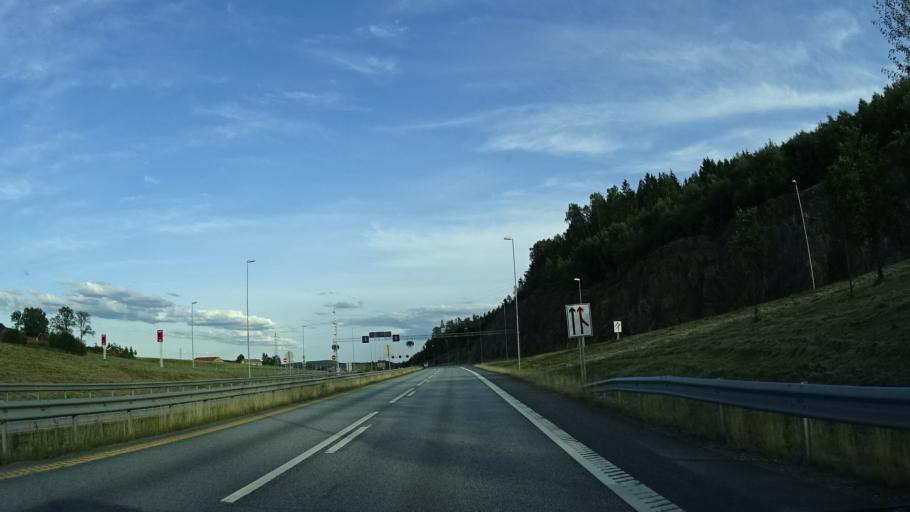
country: NO
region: Ostfold
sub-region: Spydeberg
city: Spydeberg
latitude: 59.5854
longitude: 11.1173
